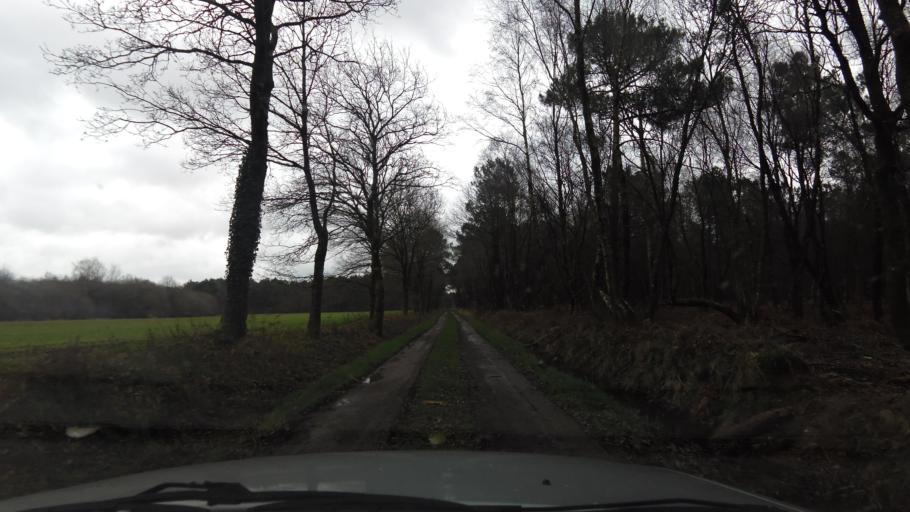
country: FR
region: Brittany
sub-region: Departement du Morbihan
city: Molac
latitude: 47.7661
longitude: -2.4837
